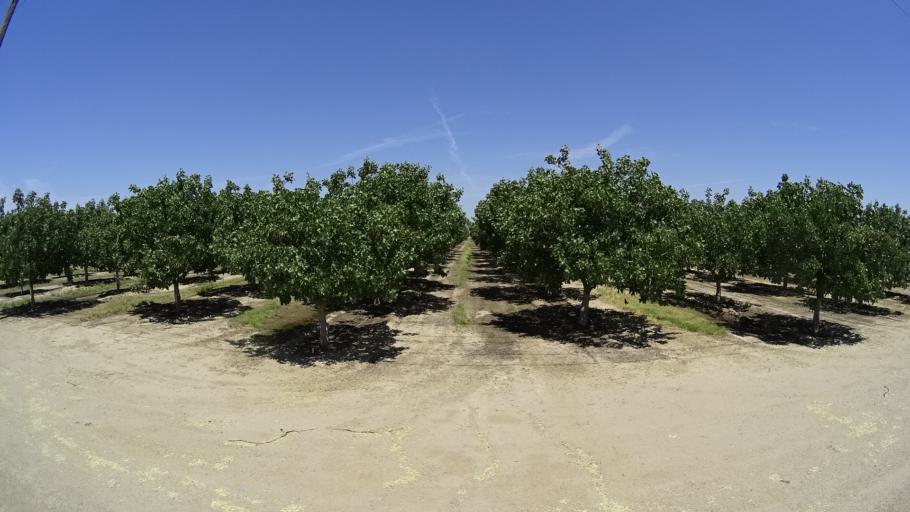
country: US
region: California
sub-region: Kings County
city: Armona
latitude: 36.2402
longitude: -119.7013
